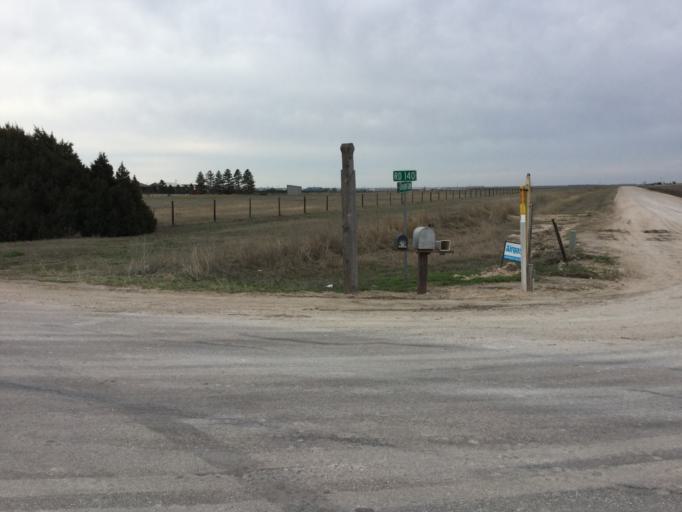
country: US
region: Kansas
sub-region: Scott County
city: Scott City
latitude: 38.4679
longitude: -100.9123
